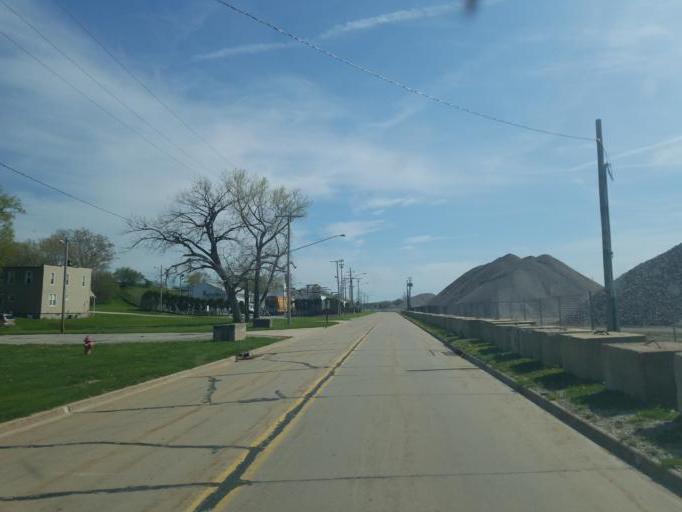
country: US
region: Ohio
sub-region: Lake County
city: Fairport Harbor
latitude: 41.7565
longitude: -81.2789
